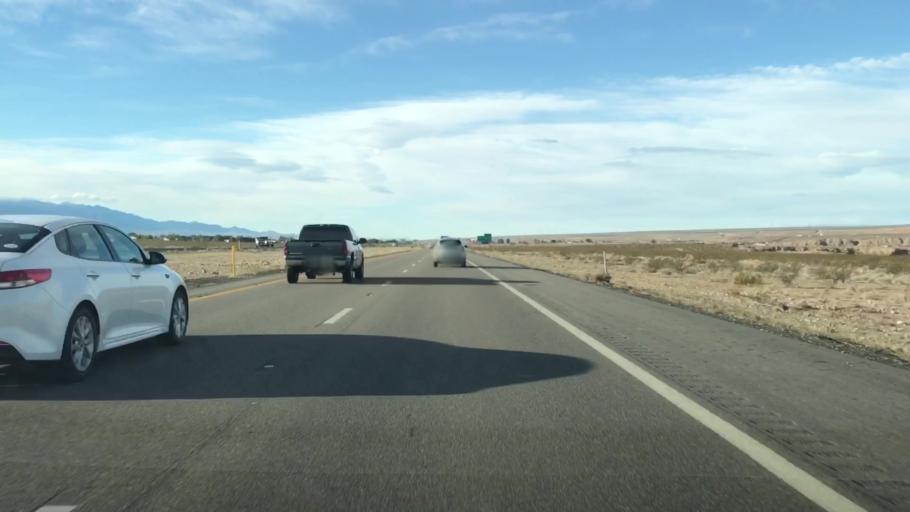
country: US
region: Arizona
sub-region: Mohave County
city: Beaver Dam
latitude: 36.9122
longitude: -113.8868
